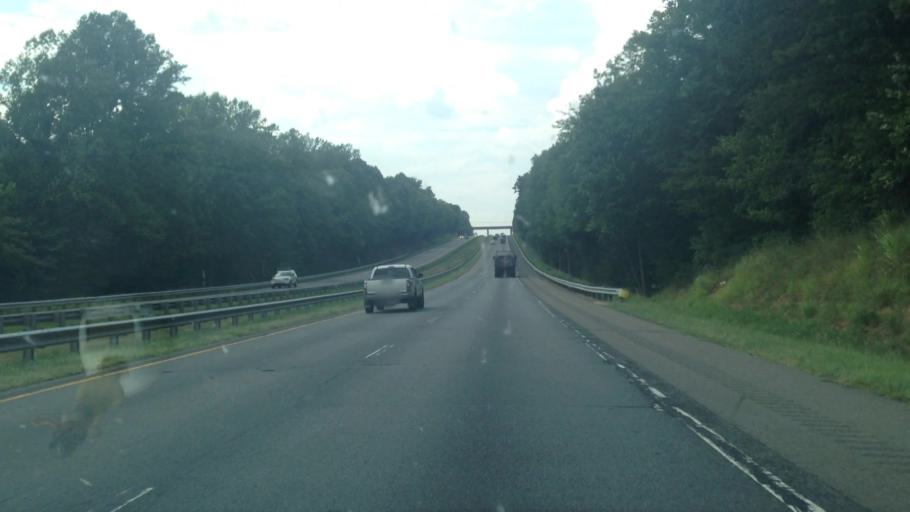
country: US
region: North Carolina
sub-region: Stokes County
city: King
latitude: 36.2792
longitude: -80.3857
